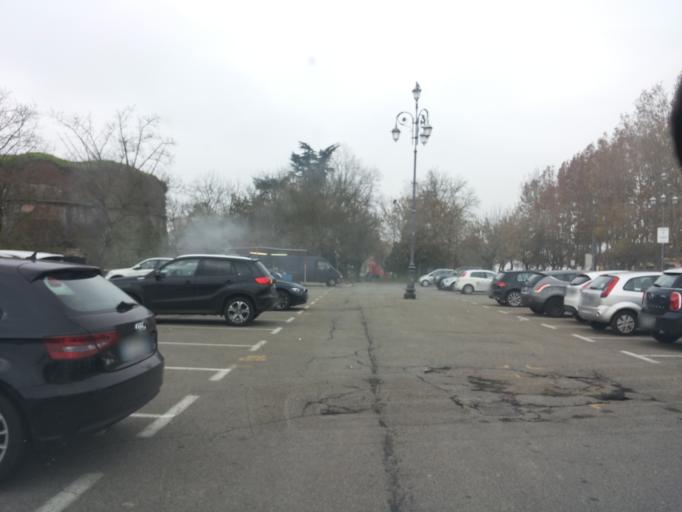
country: IT
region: Piedmont
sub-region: Provincia di Alessandria
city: Casale Monferrato
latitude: 45.1375
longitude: 8.4476
